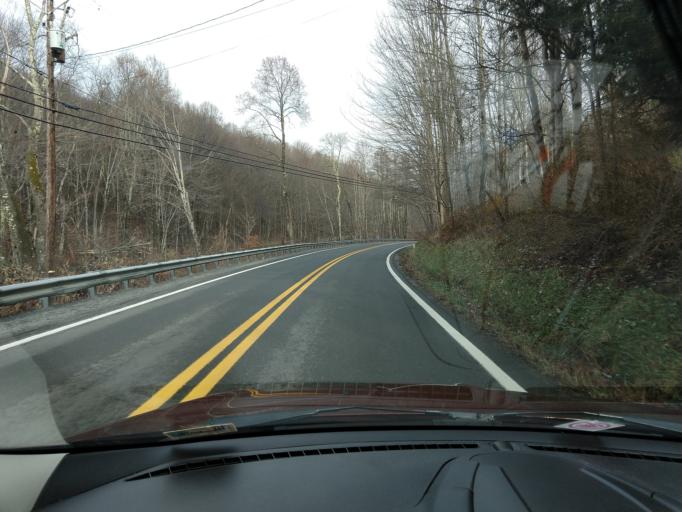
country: US
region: West Virginia
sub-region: Greenbrier County
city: Rainelle
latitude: 38.0641
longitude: -80.7084
